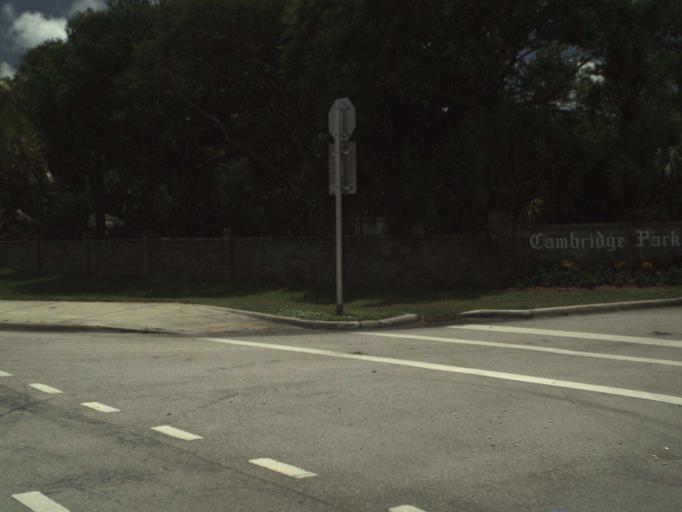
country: US
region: Florida
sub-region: Indian River County
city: West Vero Corridor
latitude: 27.6391
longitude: -80.4913
